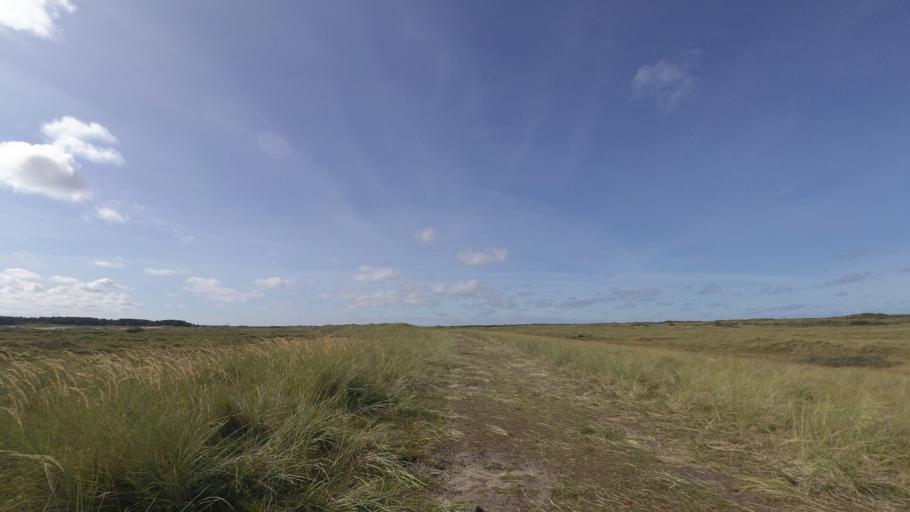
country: NL
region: Friesland
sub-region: Gemeente Ameland
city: Nes
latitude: 53.4546
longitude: 5.7080
